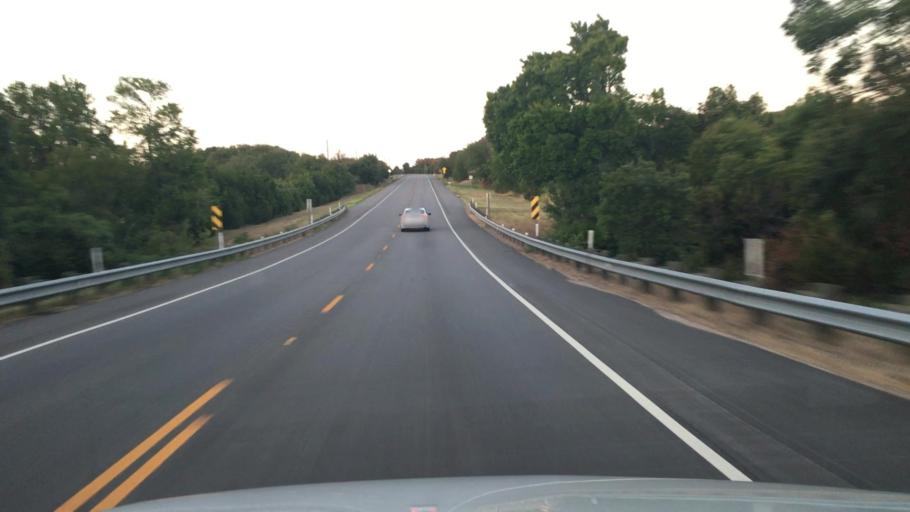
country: US
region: Texas
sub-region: Somervell County
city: Glen Rose
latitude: 32.1932
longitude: -97.8183
